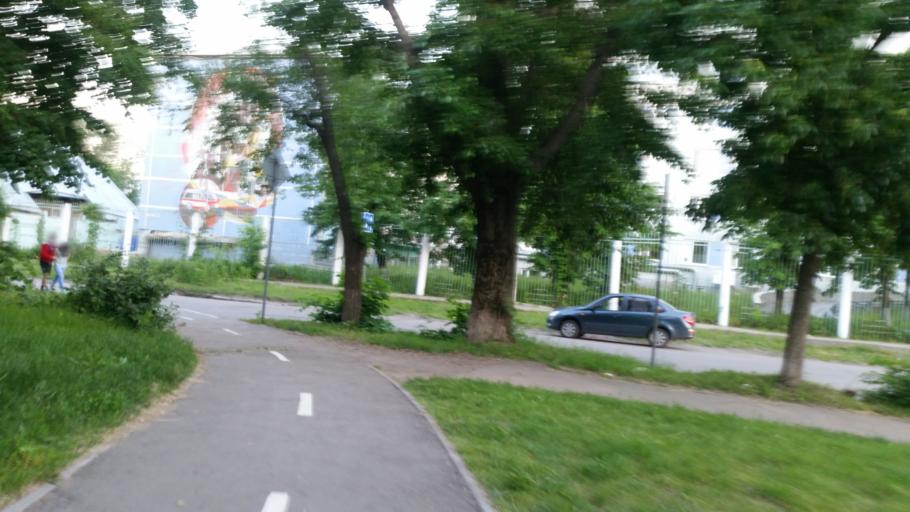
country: RU
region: Ulyanovsk
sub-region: Ulyanovskiy Rayon
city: Ulyanovsk
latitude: 54.3284
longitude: 48.4075
